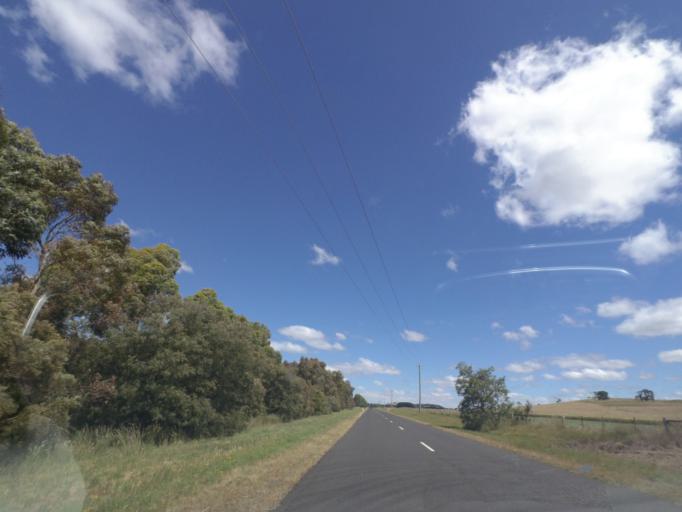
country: AU
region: Victoria
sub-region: Hume
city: Sunbury
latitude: -37.3091
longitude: 144.5167
